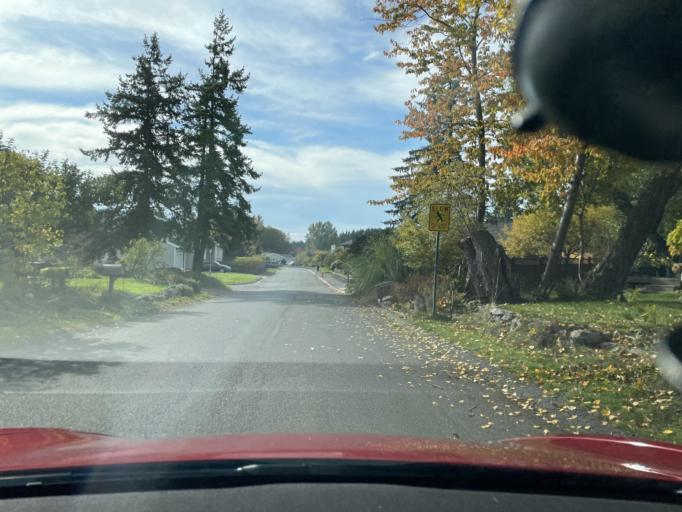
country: US
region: Washington
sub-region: San Juan County
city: Friday Harbor
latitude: 48.5283
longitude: -123.0203
